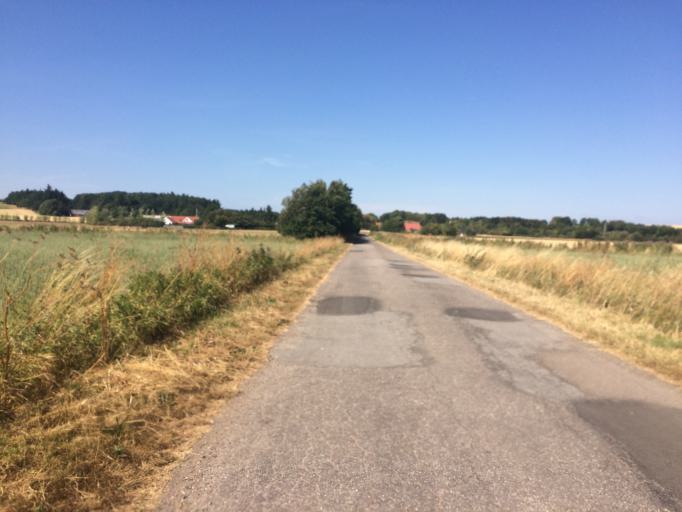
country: DK
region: Central Jutland
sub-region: Holstebro Kommune
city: Vinderup
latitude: 56.5795
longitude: 8.8258
